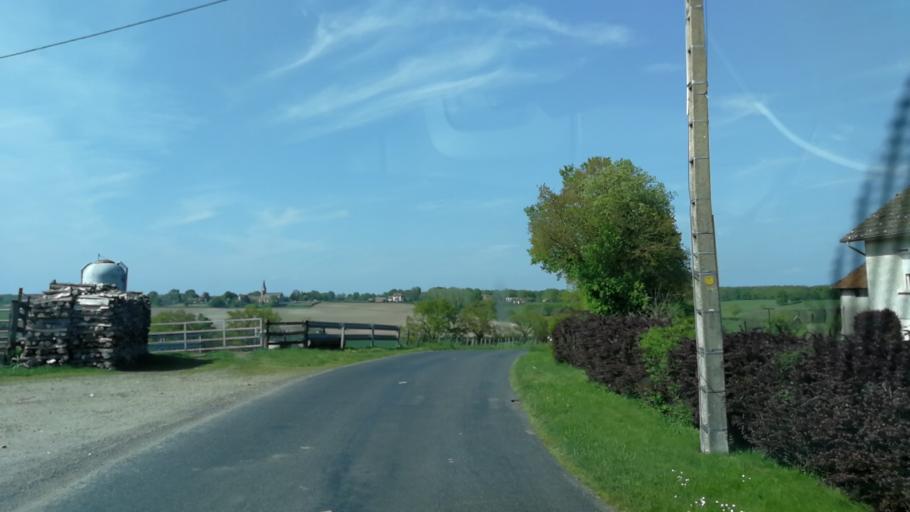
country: FR
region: Auvergne
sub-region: Departement de l'Allier
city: Saint-Gerand-le-Puy
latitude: 46.3961
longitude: 3.5797
